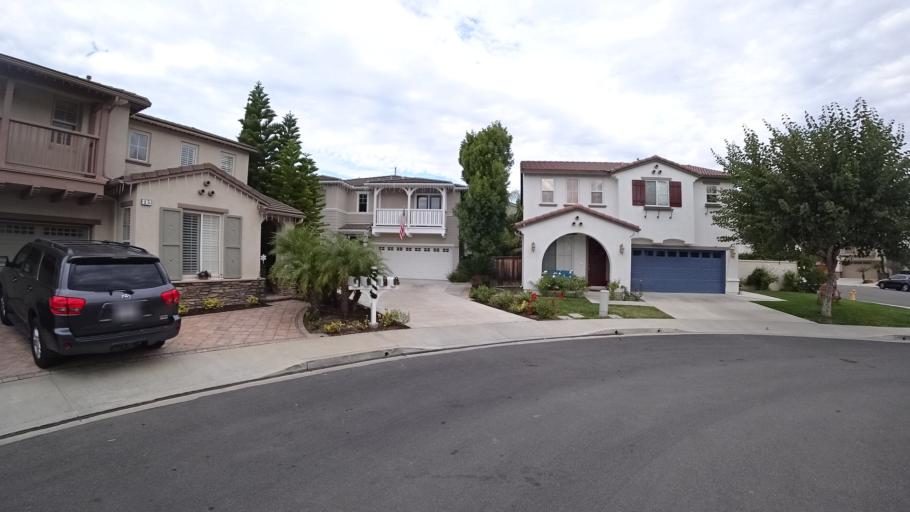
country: US
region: California
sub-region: Orange County
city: Aliso Viejo
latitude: 33.5630
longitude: -117.7411
